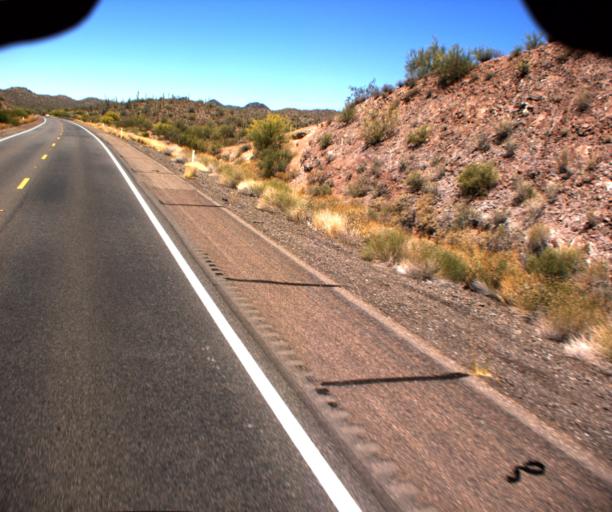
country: US
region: Arizona
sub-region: Maricopa County
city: Sun City West
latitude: 33.8355
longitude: -112.3495
